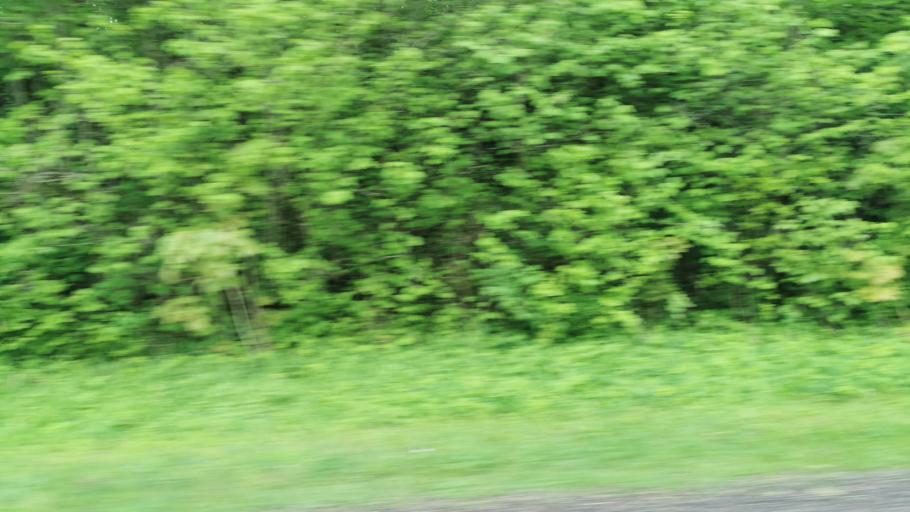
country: EE
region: Laeaene-Virumaa
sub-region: Rakvere linn
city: Rakvere
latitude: 59.2706
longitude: 26.3541
